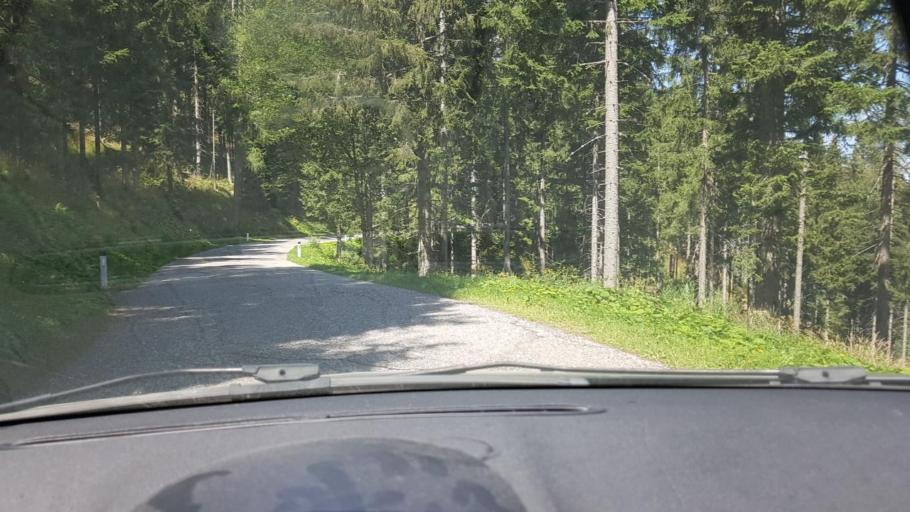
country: AT
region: Carinthia
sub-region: Politischer Bezirk Volkermarkt
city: Bad Eisenkappel
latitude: 46.4244
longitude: 14.5804
